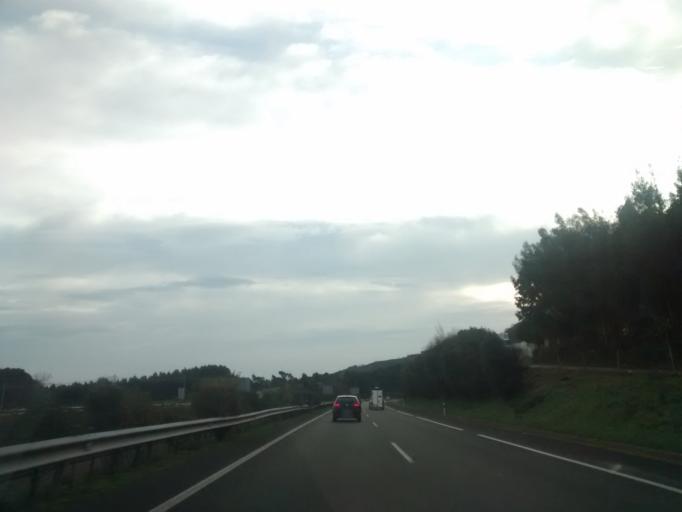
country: ES
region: Cantabria
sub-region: Provincia de Cantabria
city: Castro-Urdiales
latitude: 43.4015
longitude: -3.2860
